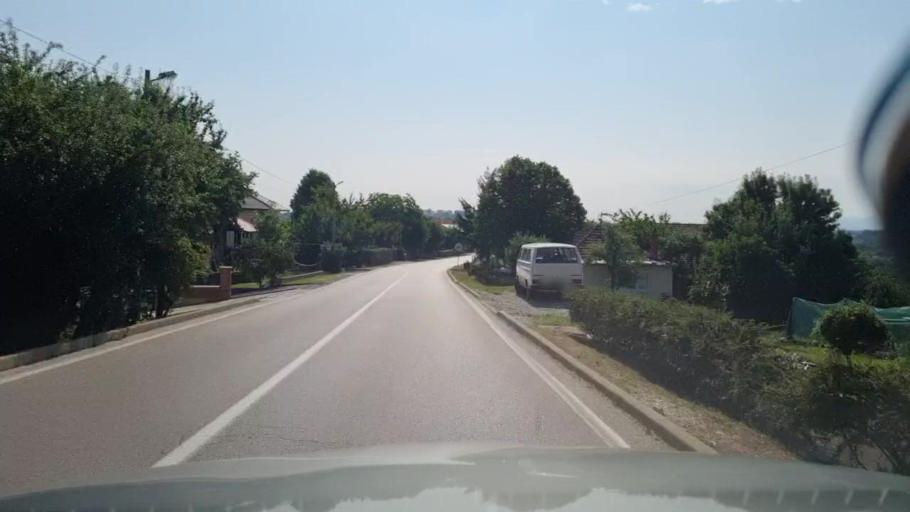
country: BA
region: Federation of Bosnia and Herzegovina
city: Mionica
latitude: 44.8679
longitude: 18.4559
